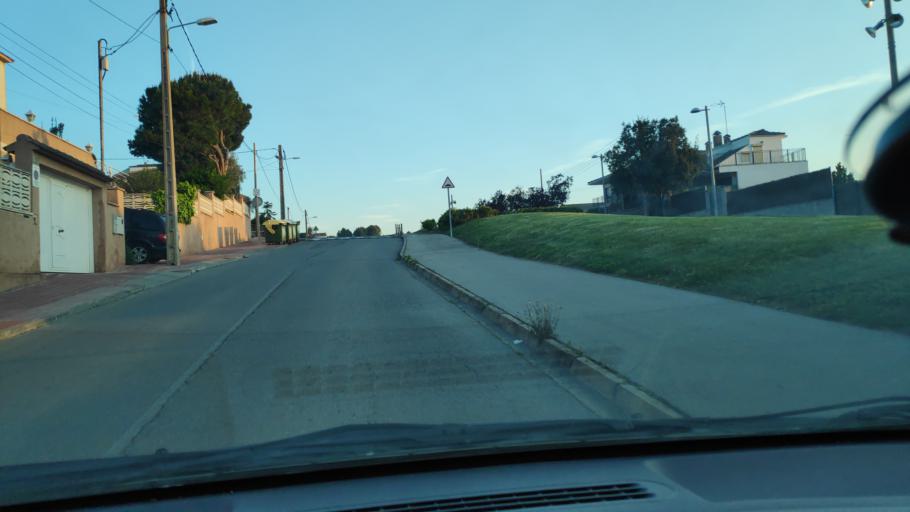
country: ES
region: Catalonia
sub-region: Provincia de Barcelona
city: Sant Quirze del Valles
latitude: 41.5376
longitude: 2.0482
